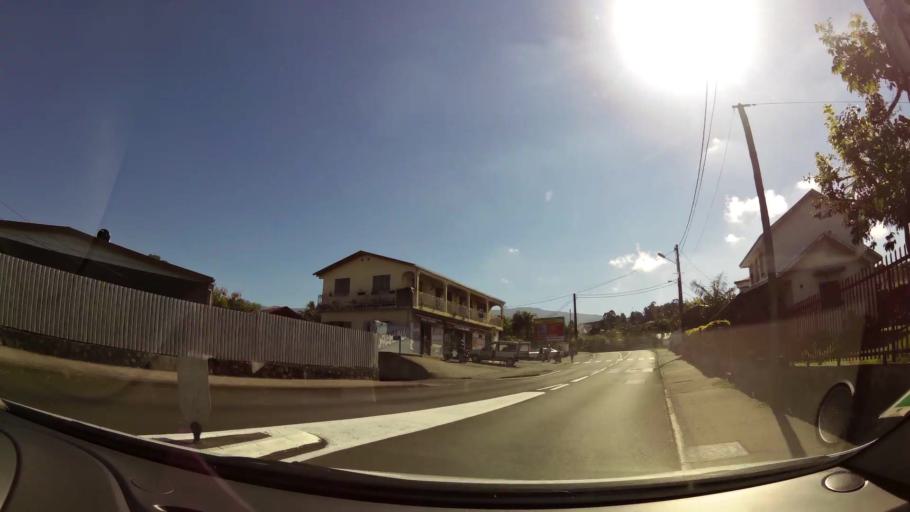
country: RE
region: Reunion
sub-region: Reunion
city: Le Tampon
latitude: -21.2645
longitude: 55.5078
